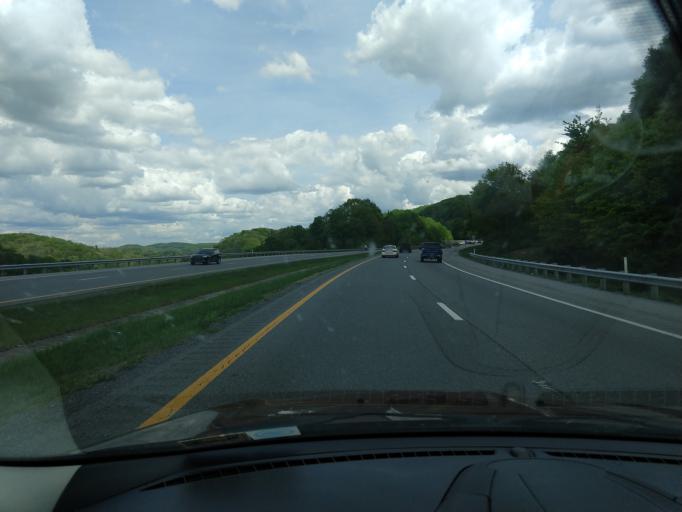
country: US
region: West Virginia
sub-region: Mercer County
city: Bluefield
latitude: 37.2954
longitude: -81.1606
